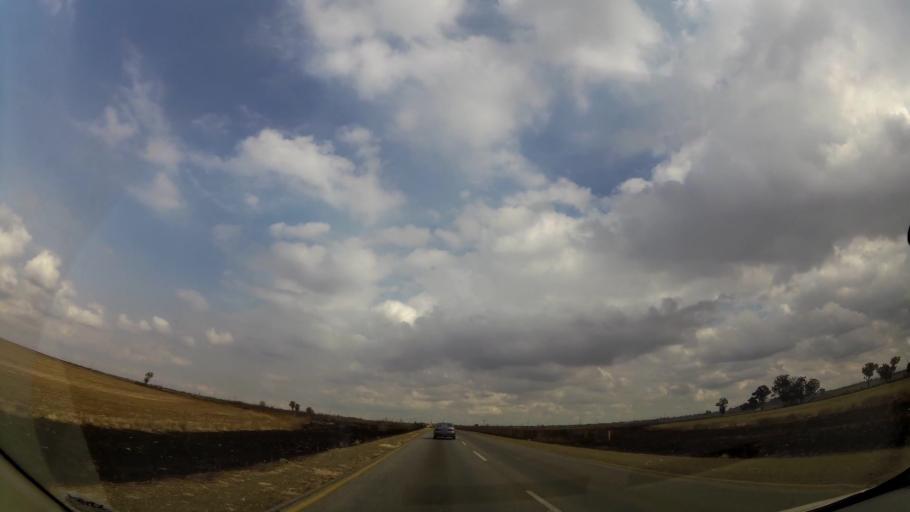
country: ZA
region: Orange Free State
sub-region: Fezile Dabi District Municipality
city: Sasolburg
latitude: -26.8390
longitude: 27.8940
